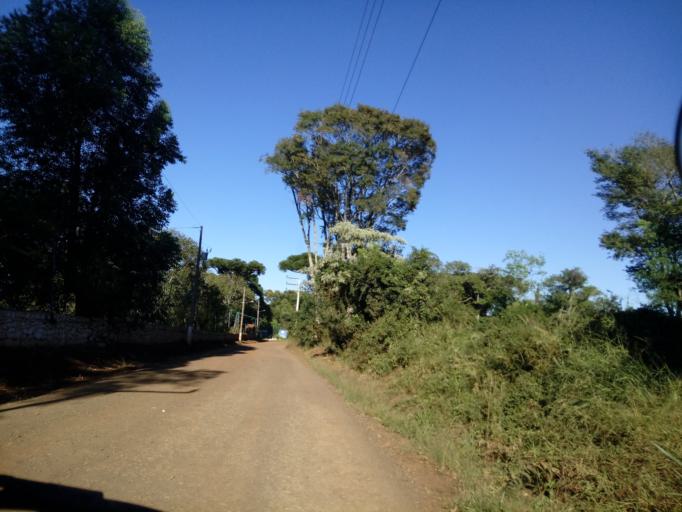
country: BR
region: Santa Catarina
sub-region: Chapeco
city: Chapeco
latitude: -27.1942
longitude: -52.6683
